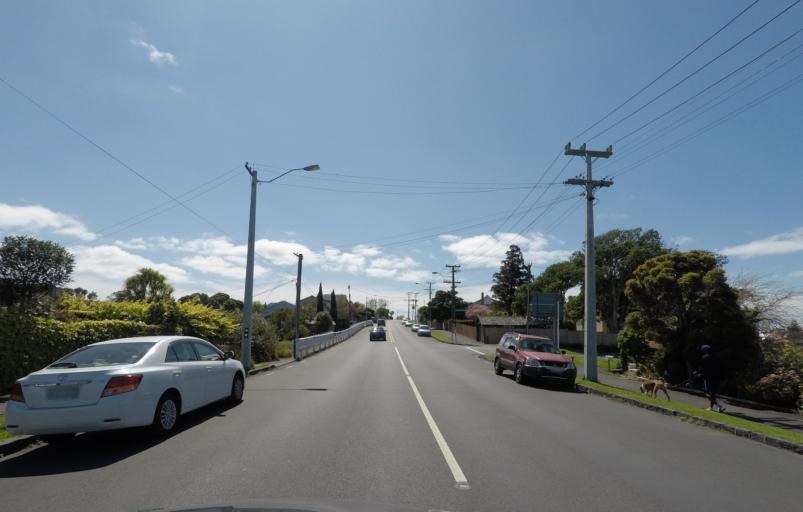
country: NZ
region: Auckland
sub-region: Auckland
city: Auckland
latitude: -36.8858
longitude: 174.8093
